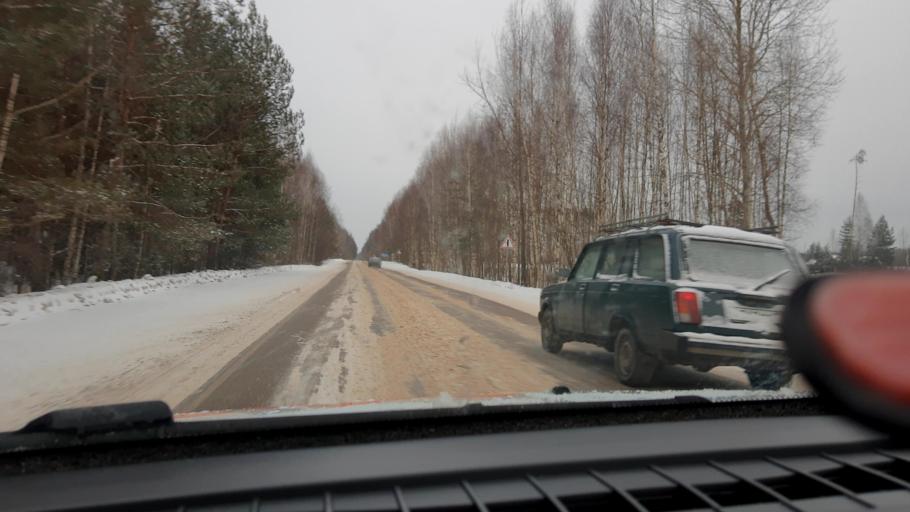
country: RU
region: Nizjnij Novgorod
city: Pamyat' Parizhskoy Kommuny
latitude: 56.2742
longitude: 44.4032
